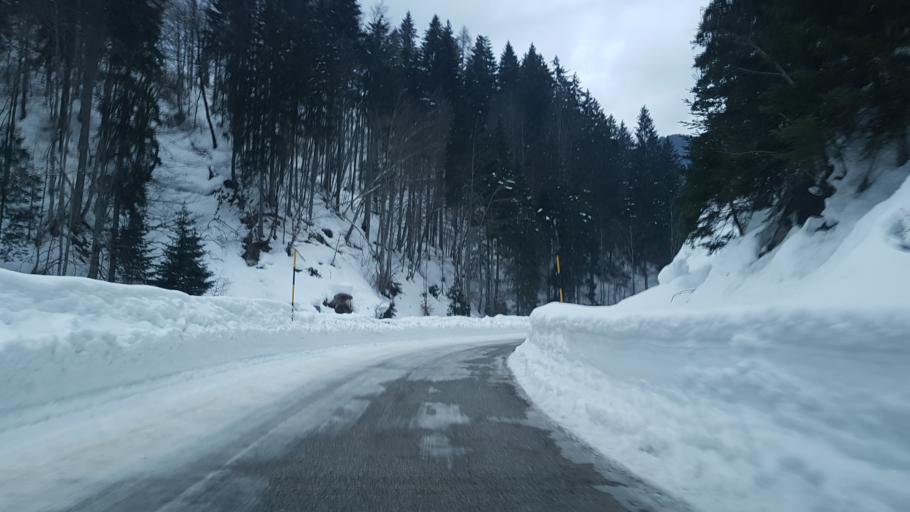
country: IT
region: Friuli Venezia Giulia
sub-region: Provincia di Udine
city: Malborghetto
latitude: 46.5294
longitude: 13.4722
